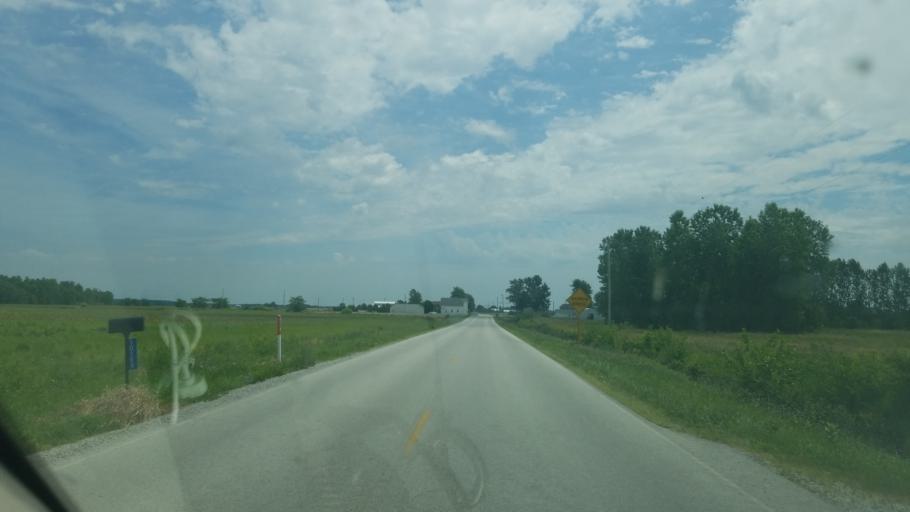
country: US
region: Ohio
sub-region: Wood County
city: Bowling Green
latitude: 41.2968
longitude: -83.5970
